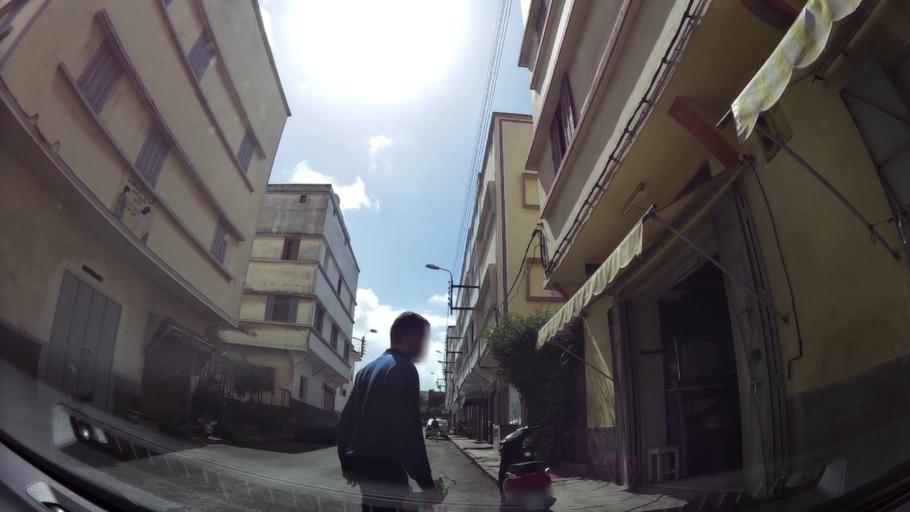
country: MA
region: Grand Casablanca
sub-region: Casablanca
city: Casablanca
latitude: 33.5396
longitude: -7.5839
